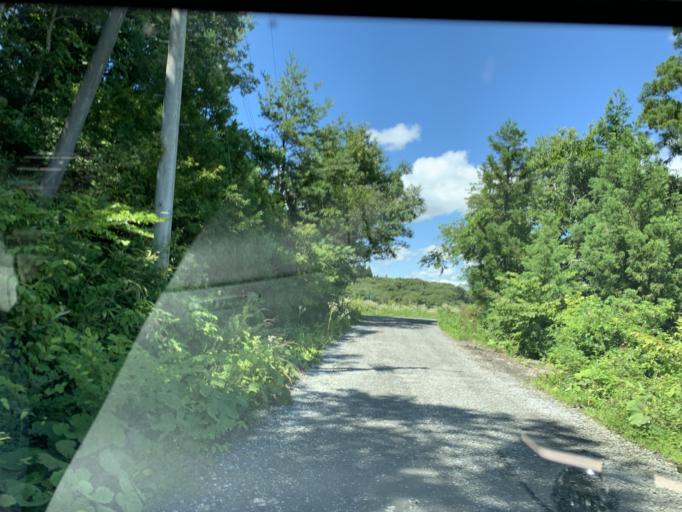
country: JP
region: Iwate
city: Ichinoseki
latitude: 38.9262
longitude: 141.0577
